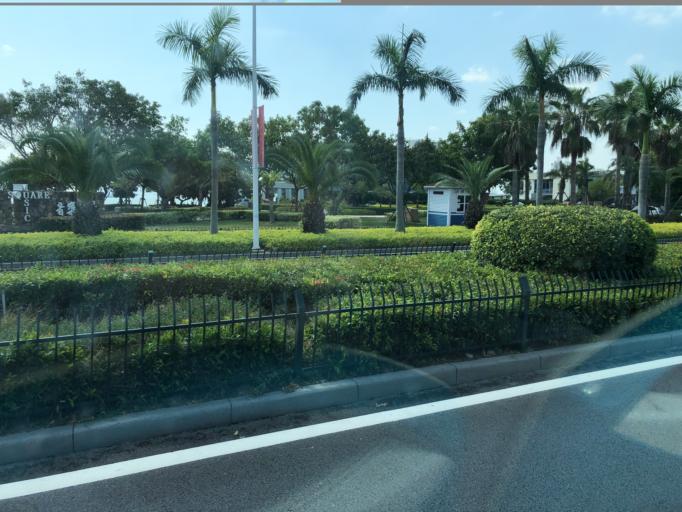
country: CN
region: Fujian
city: Xiamen
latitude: 24.4269
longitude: 118.1230
